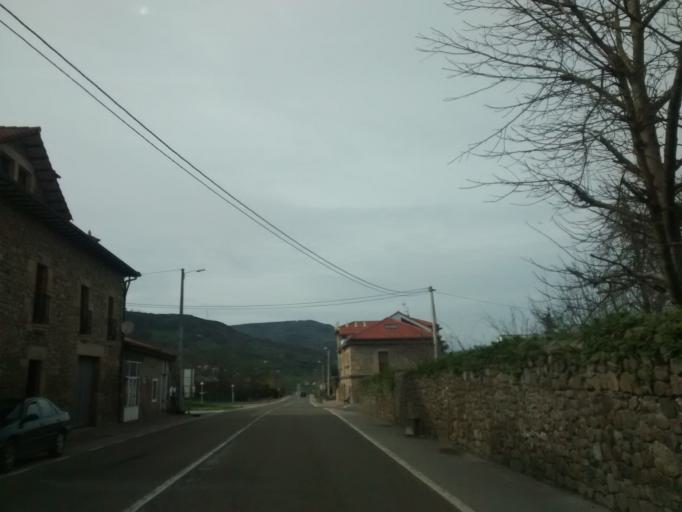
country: ES
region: Cantabria
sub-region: Provincia de Cantabria
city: Santiurde de Toranzo
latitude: 43.2119
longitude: -3.9388
